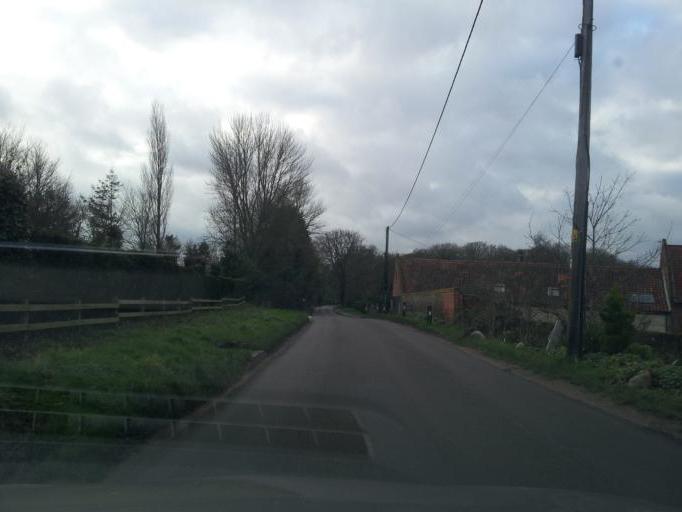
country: GB
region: England
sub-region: Norfolk
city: Lingwood
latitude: 52.6183
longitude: 1.4751
